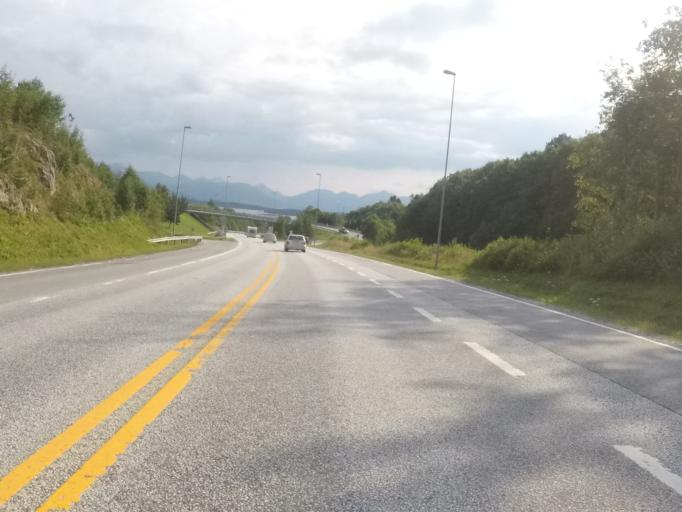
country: NO
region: More og Romsdal
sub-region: Molde
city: Molde
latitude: 62.7538
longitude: 7.2638
